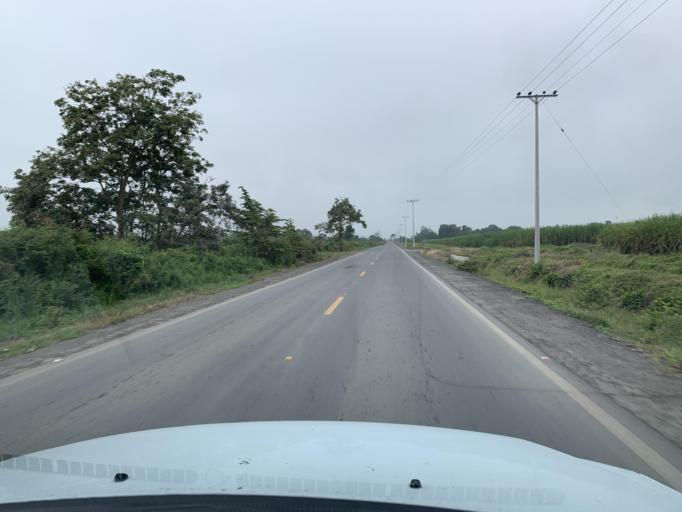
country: EC
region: Guayas
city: Coronel Marcelino Mariduena
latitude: -2.3301
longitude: -79.5254
